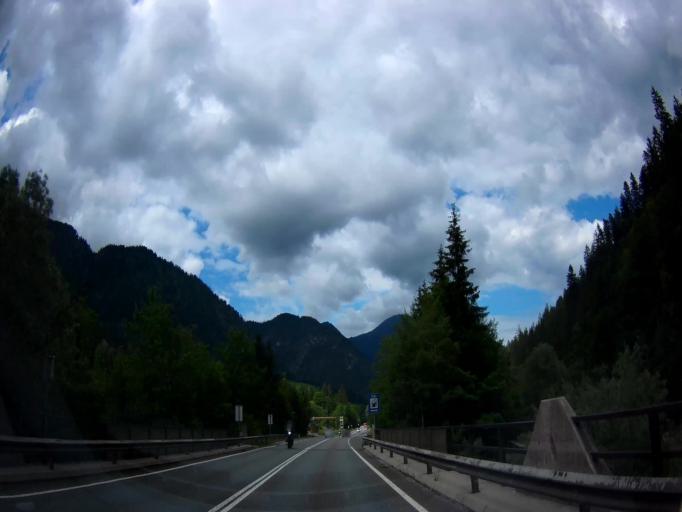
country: AT
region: Salzburg
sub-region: Politischer Bezirk Zell am See
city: Unken
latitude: 47.6496
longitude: 12.7369
